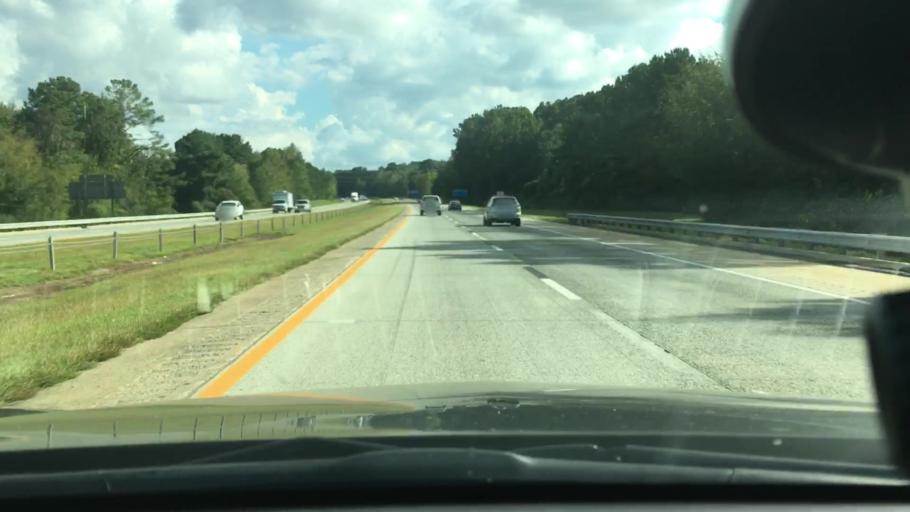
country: US
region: North Carolina
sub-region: Orange County
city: Chapel Hill
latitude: 35.9802
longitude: -79.0720
